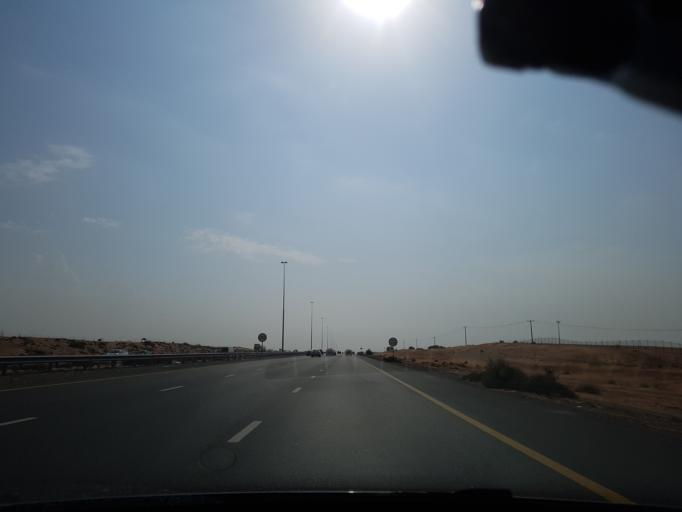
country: AE
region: Umm al Qaywayn
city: Umm al Qaywayn
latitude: 25.5229
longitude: 55.7171
